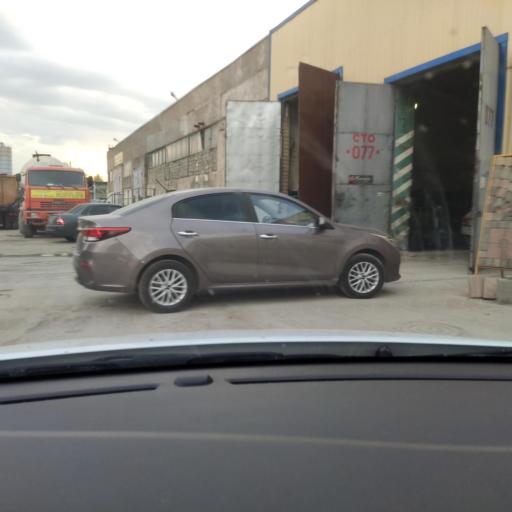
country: RU
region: Tatarstan
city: Verkhniy Uslon
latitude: 55.8035
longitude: 49.0436
